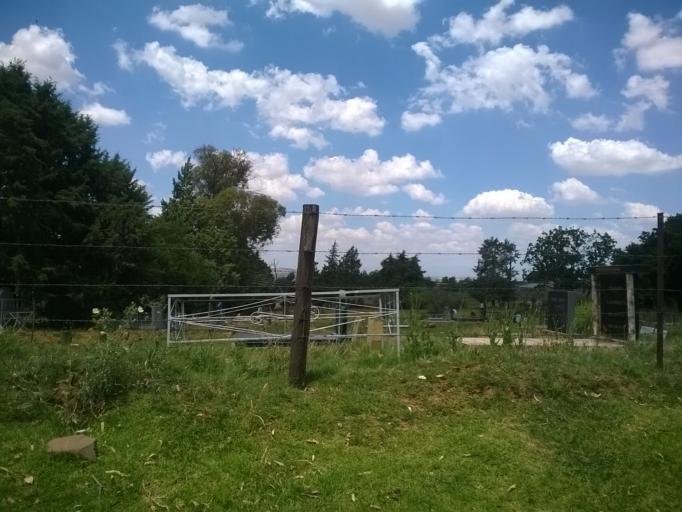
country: LS
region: Berea
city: Teyateyaneng
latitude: -29.1479
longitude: 27.7554
